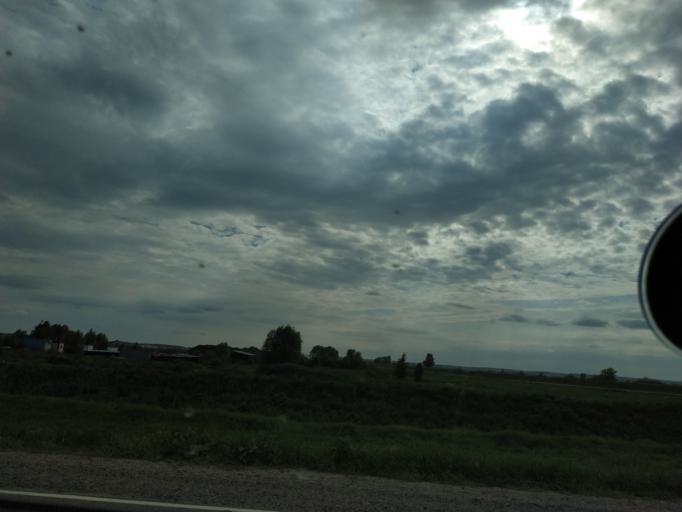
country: RU
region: Moskovskaya
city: Ramenskoye
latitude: 55.5128
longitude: 38.2782
